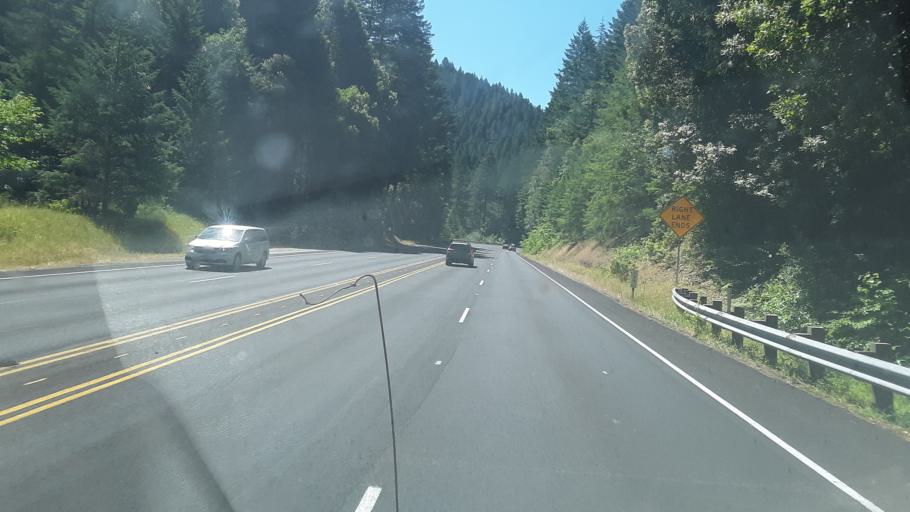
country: US
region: Oregon
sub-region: Josephine County
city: Cave Junction
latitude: 41.9108
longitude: -123.7699
